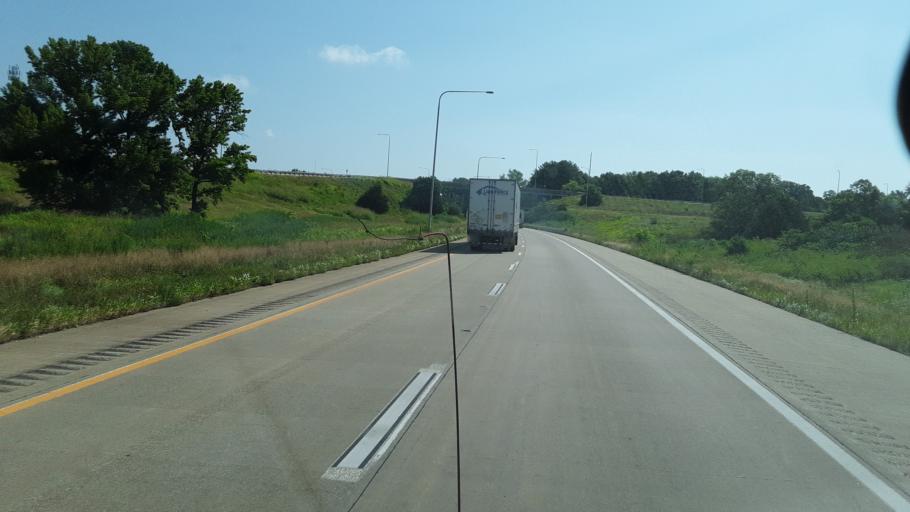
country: US
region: Illinois
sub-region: Effingham County
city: Effingham
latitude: 39.0928
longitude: -88.5845
